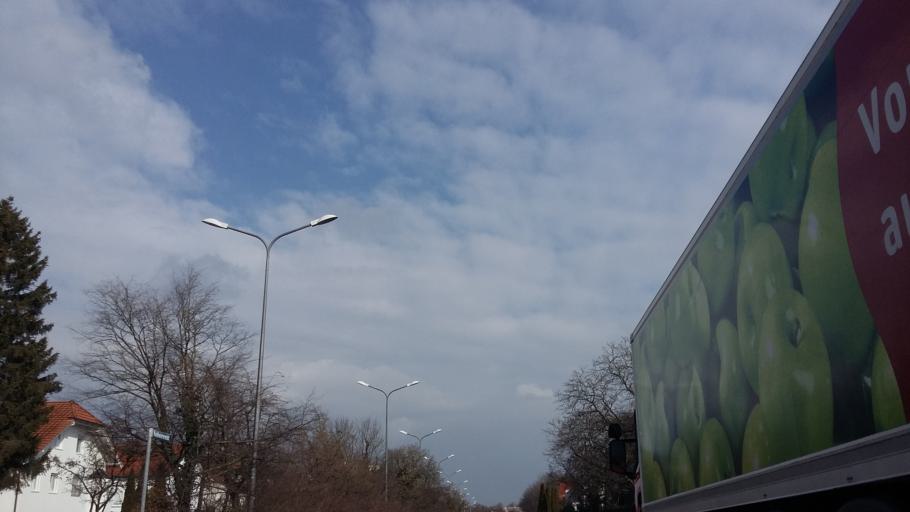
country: DE
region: Bavaria
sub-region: Upper Bavaria
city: Neuried
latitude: 48.1203
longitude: 11.4786
